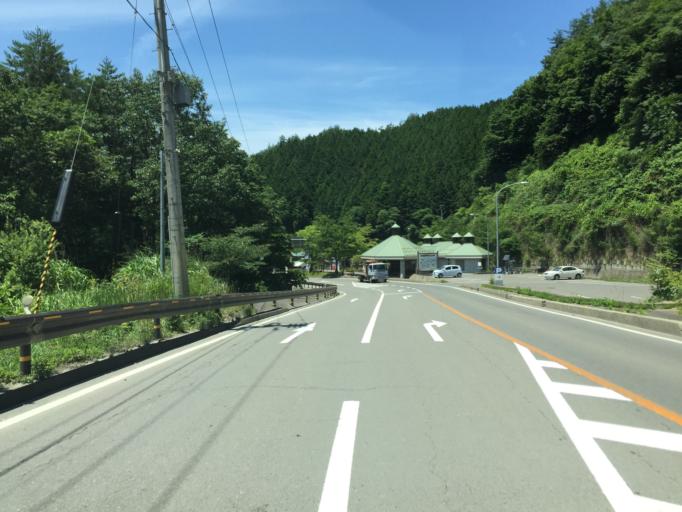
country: JP
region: Fukushima
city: Yanagawamachi-saiwaicho
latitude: 37.7547
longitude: 140.6886
